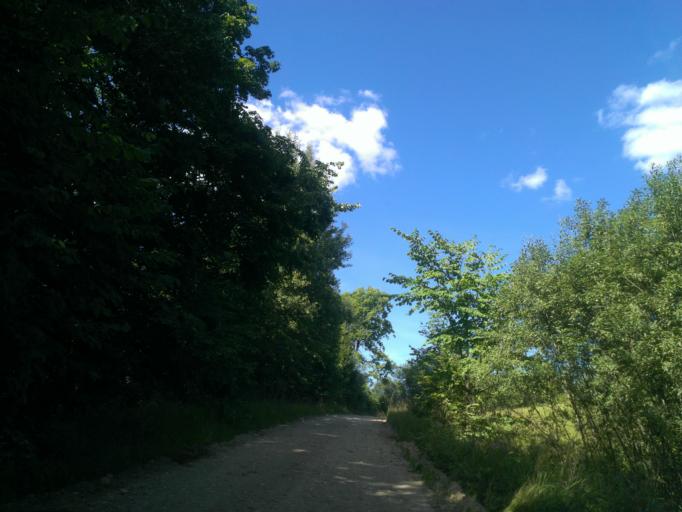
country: LV
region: Malpils
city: Malpils
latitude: 57.0131
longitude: 24.9895
